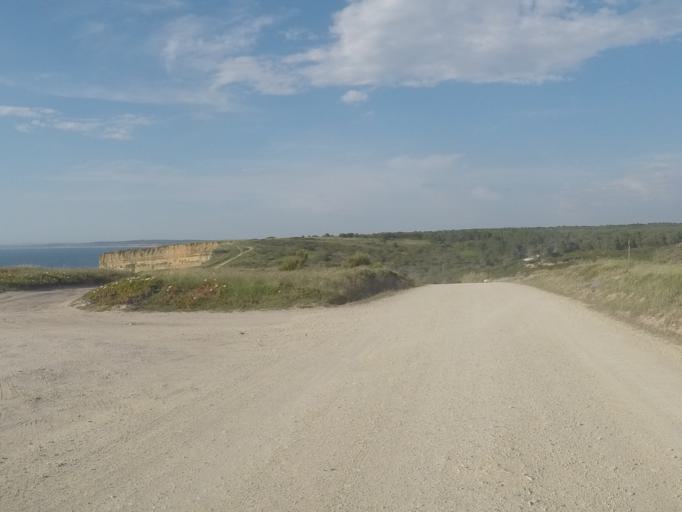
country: PT
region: Setubal
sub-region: Sesimbra
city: Sesimbra
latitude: 38.4501
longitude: -9.1994
